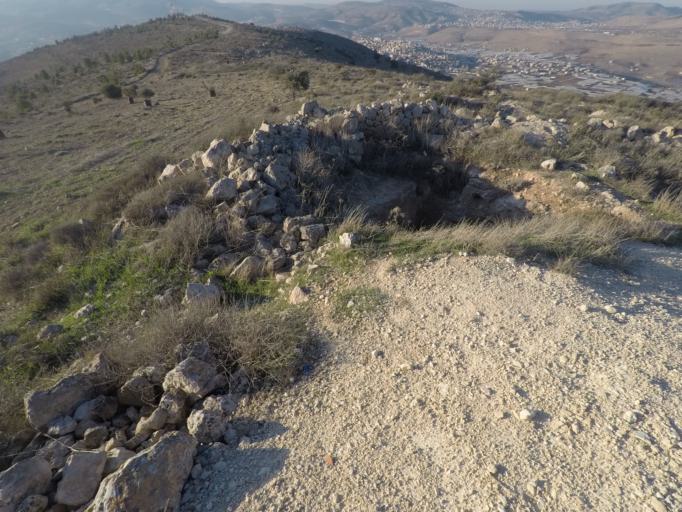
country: PS
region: West Bank
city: Tammun
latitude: 32.2643
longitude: 35.3976
